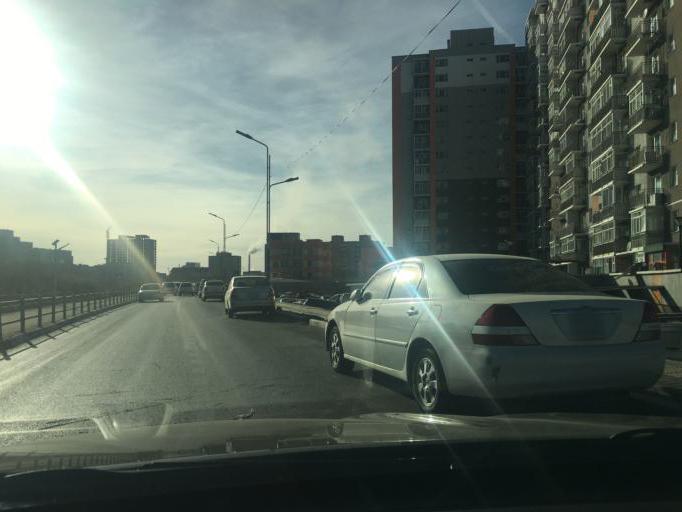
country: MN
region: Ulaanbaatar
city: Ulaanbaatar
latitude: 47.9038
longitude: 106.9017
